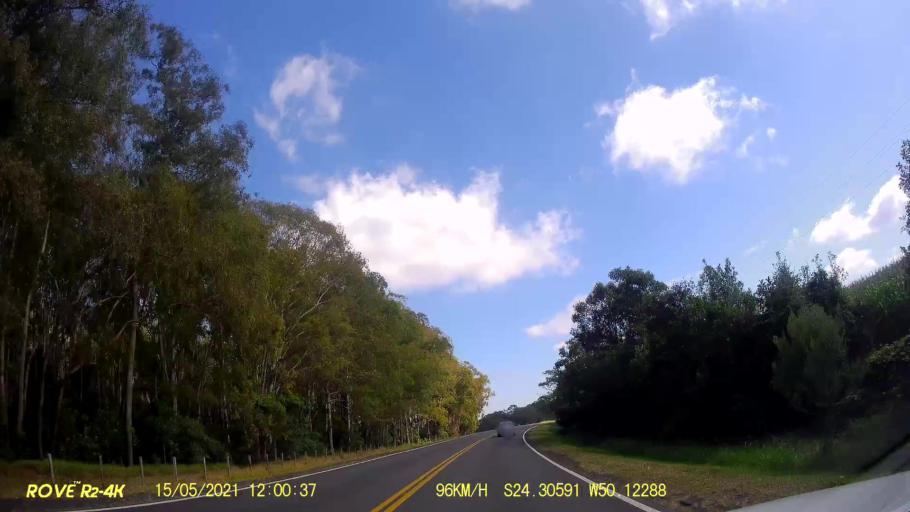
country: BR
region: Parana
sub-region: Pirai Do Sul
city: Pirai do Sul
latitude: -24.3058
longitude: -50.1231
